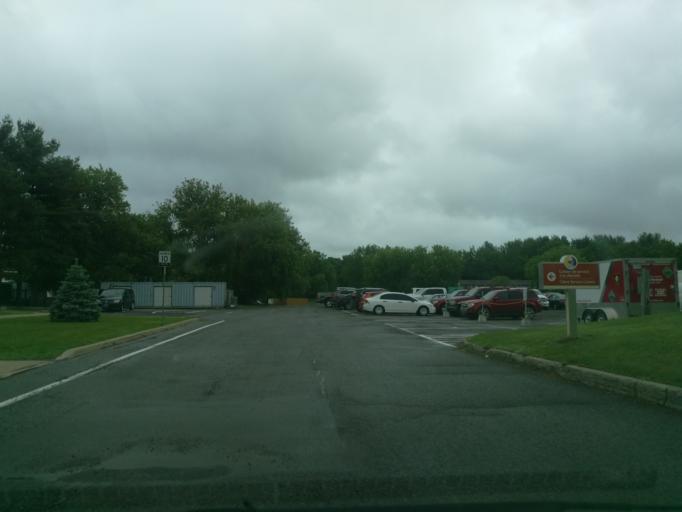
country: CA
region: Ontario
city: Clarence-Rockland
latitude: 45.5508
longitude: -75.2896
